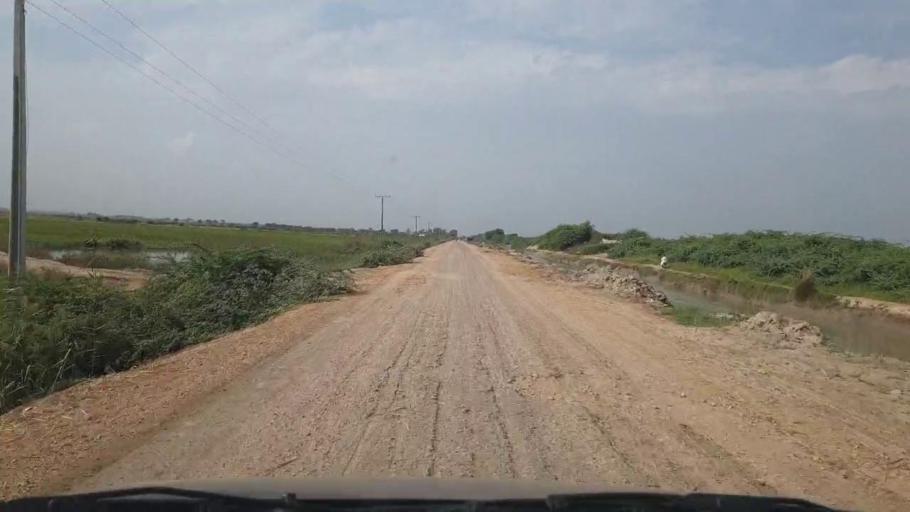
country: PK
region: Sindh
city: Kario
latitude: 24.6256
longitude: 68.5771
